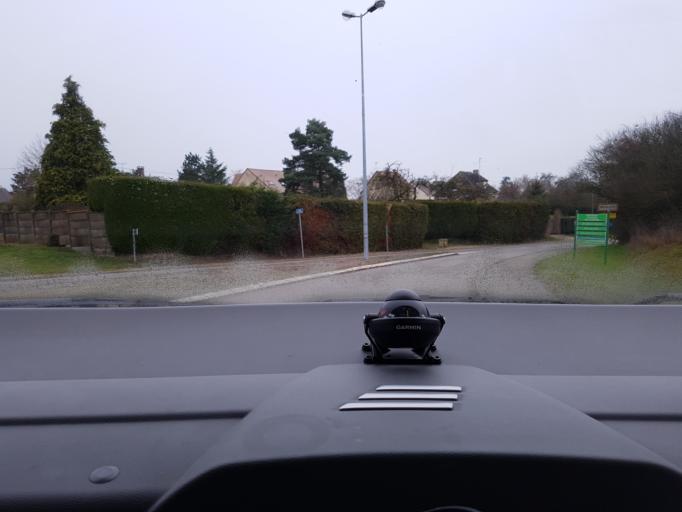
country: FR
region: Haute-Normandie
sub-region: Departement de l'Eure
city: Rugles
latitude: 48.8160
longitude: 0.7055
